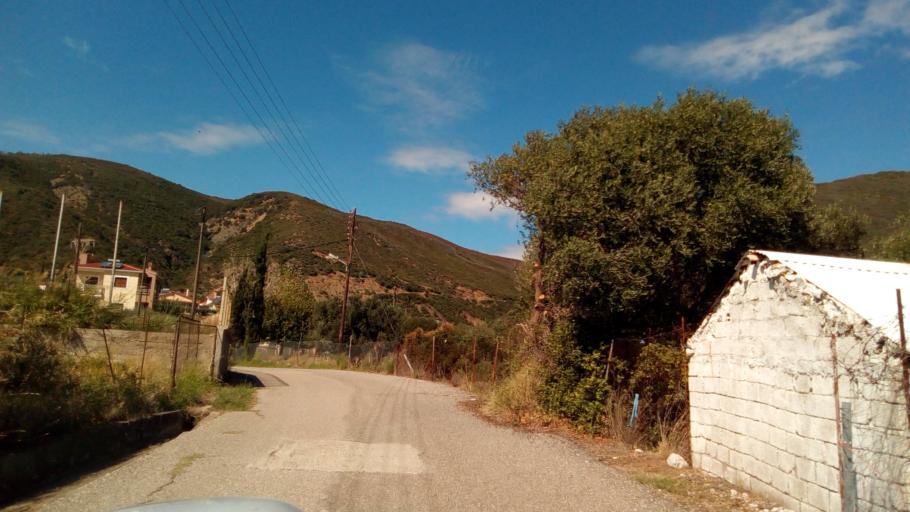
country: GR
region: West Greece
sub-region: Nomos Aitolias kai Akarnanias
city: Antirrio
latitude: 38.3713
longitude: 21.7753
